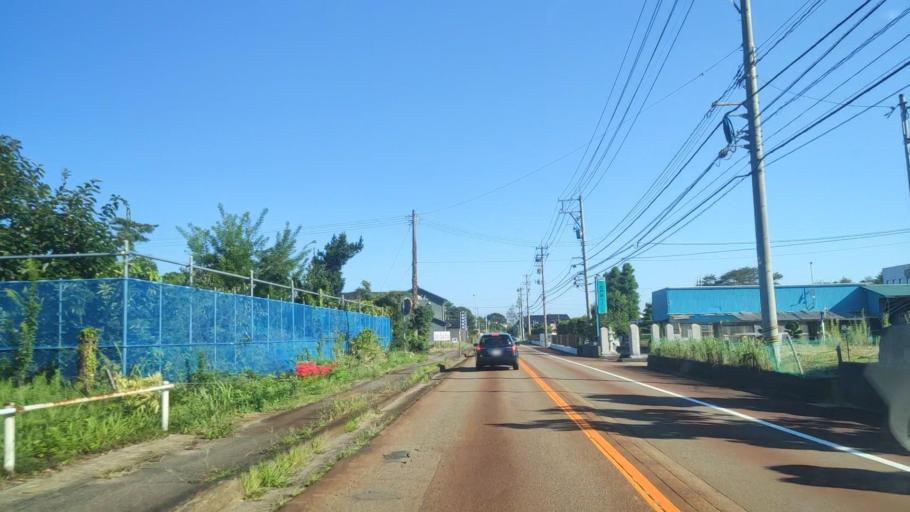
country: JP
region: Ishikawa
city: Hakui
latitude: 36.8550
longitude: 136.7694
